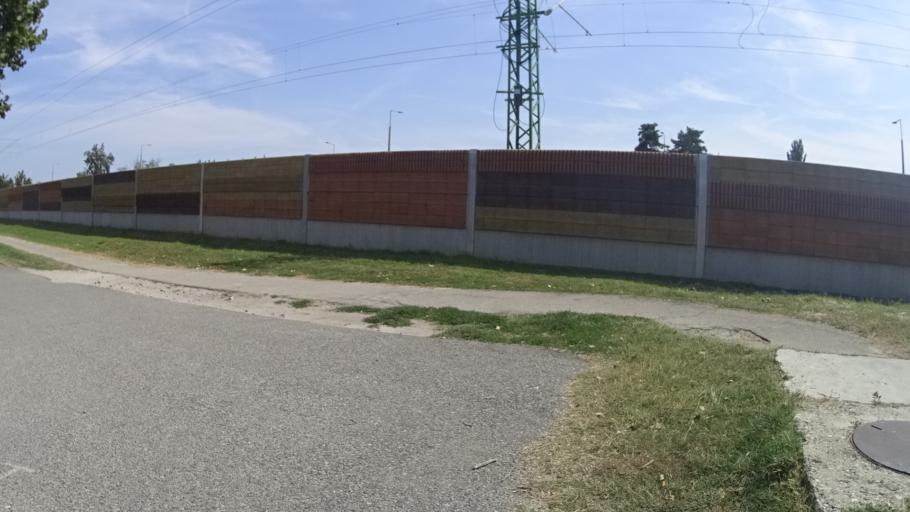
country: HU
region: Somogy
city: Balatonboglar
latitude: 46.7676
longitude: 17.6193
